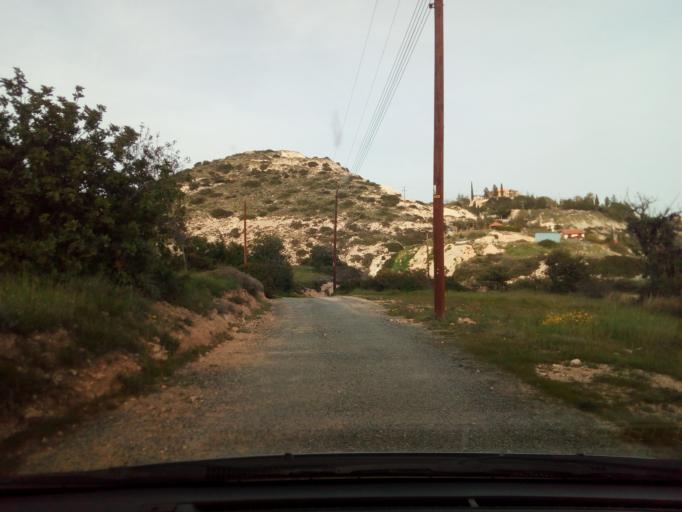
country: CY
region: Larnaka
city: Agios Tychon
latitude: 34.7226
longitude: 33.1271
